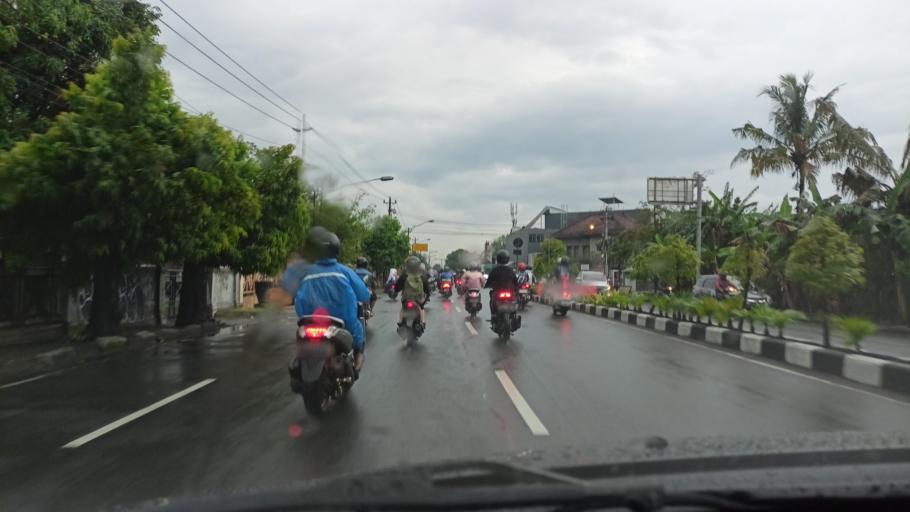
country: ID
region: Central Java
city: Surakarta
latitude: -7.5524
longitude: 110.8019
